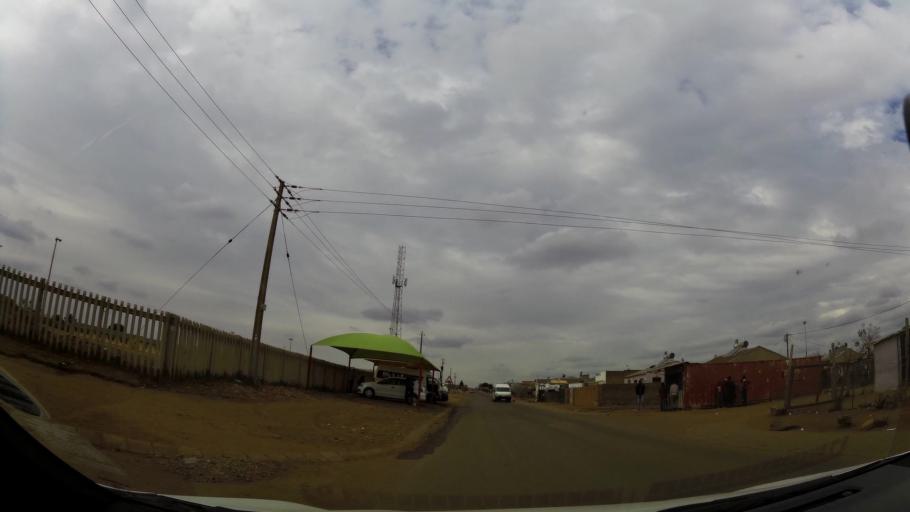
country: ZA
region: Gauteng
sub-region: Ekurhuleni Metropolitan Municipality
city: Germiston
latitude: -26.3923
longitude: 28.1305
